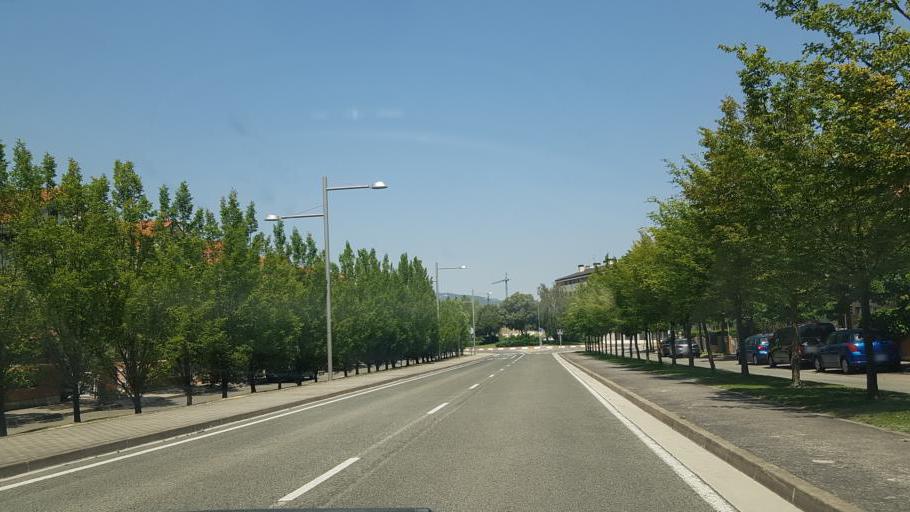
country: ES
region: Navarre
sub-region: Provincia de Navarra
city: Segundo Ensanche
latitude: 42.7949
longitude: -1.6218
